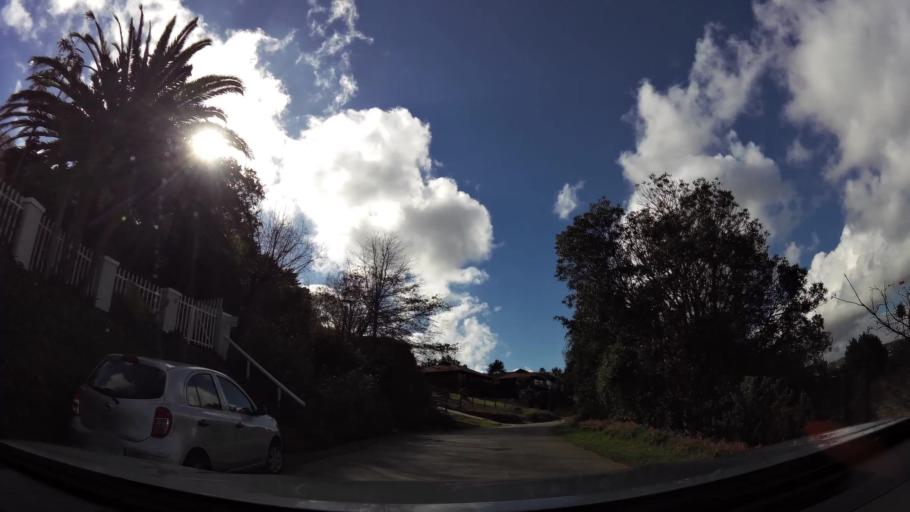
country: ZA
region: Western Cape
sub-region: Eden District Municipality
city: Knysna
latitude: -34.0376
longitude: 23.0677
